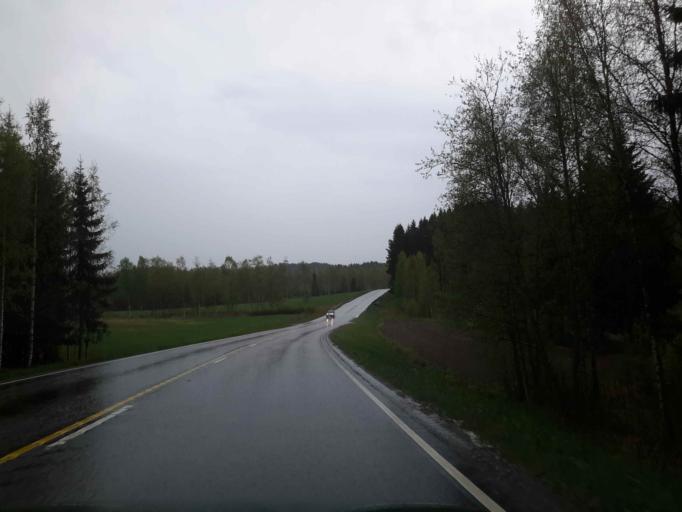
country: FI
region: Uusimaa
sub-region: Helsinki
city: Vihti
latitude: 60.3867
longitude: 24.5111
